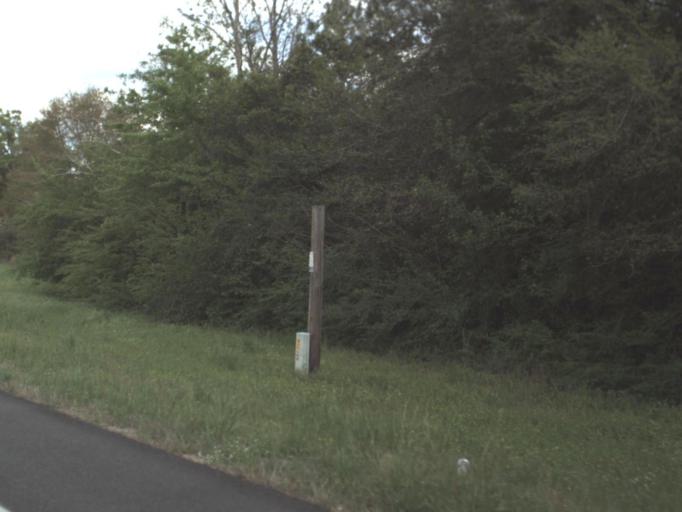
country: US
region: Florida
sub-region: Okaloosa County
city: Crestview
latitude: 30.8701
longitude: -86.5236
